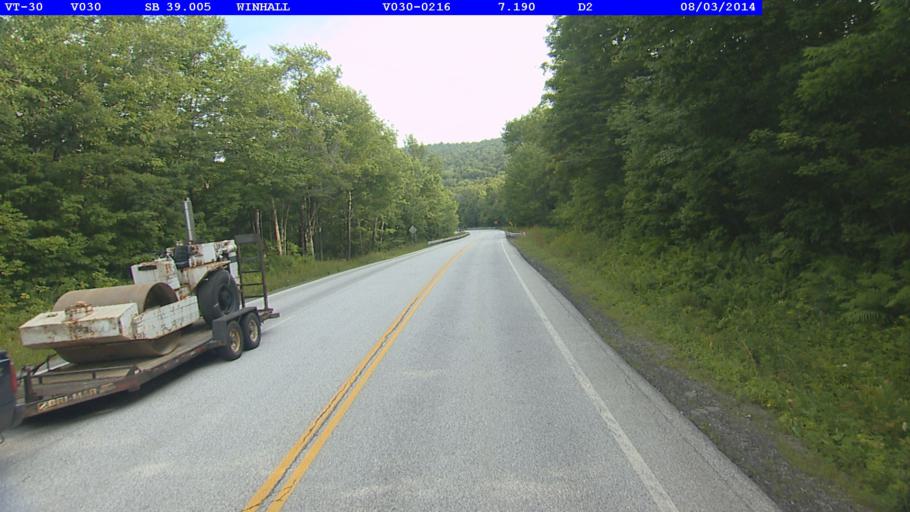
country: US
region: Vermont
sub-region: Bennington County
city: Manchester Center
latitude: 43.1992
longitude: -72.9594
